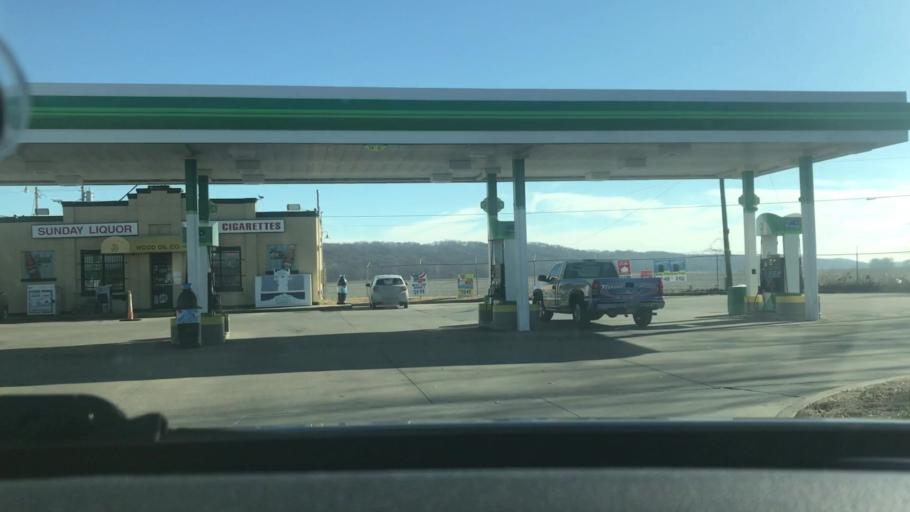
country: US
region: Missouri
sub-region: Platte County
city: Weston
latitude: 39.3622
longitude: -94.8776
